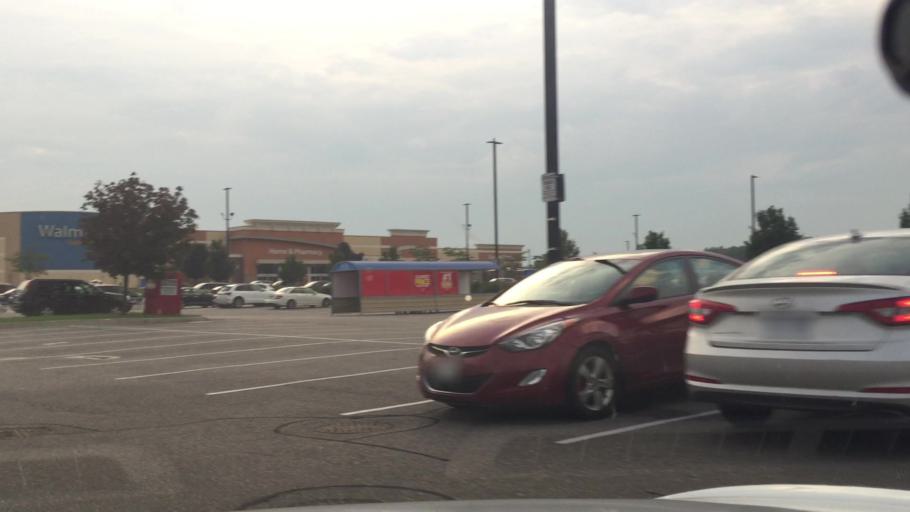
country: CA
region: Ontario
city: Markham
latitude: 43.8712
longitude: -79.2135
